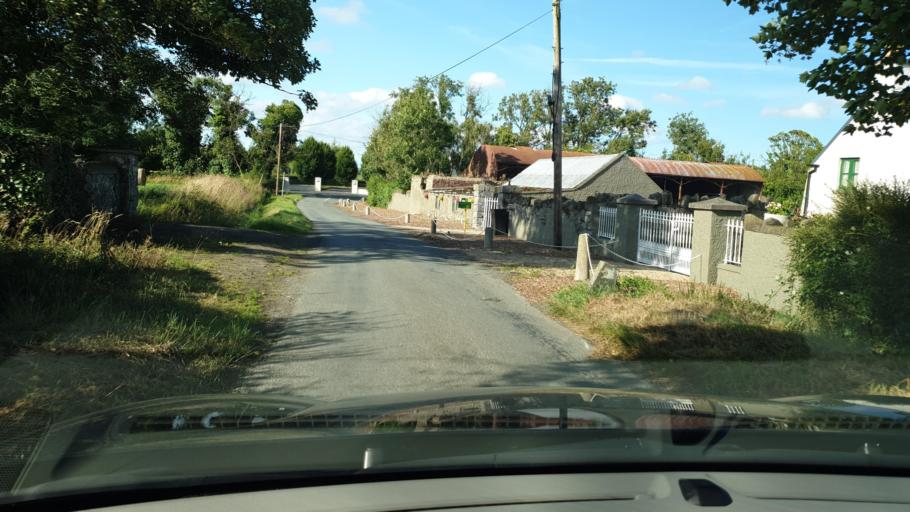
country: IE
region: Leinster
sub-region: An Mhi
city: Ashbourne
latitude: 53.5356
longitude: -6.3575
